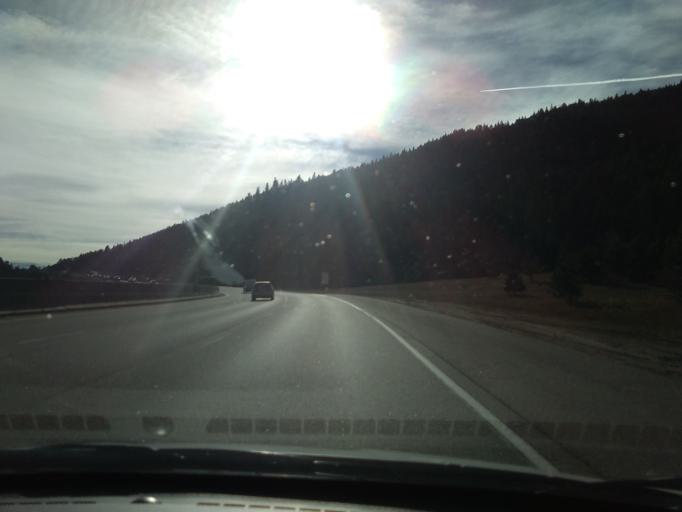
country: US
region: Colorado
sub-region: Clear Creek County
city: Idaho Springs
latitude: 39.7313
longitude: -105.4268
